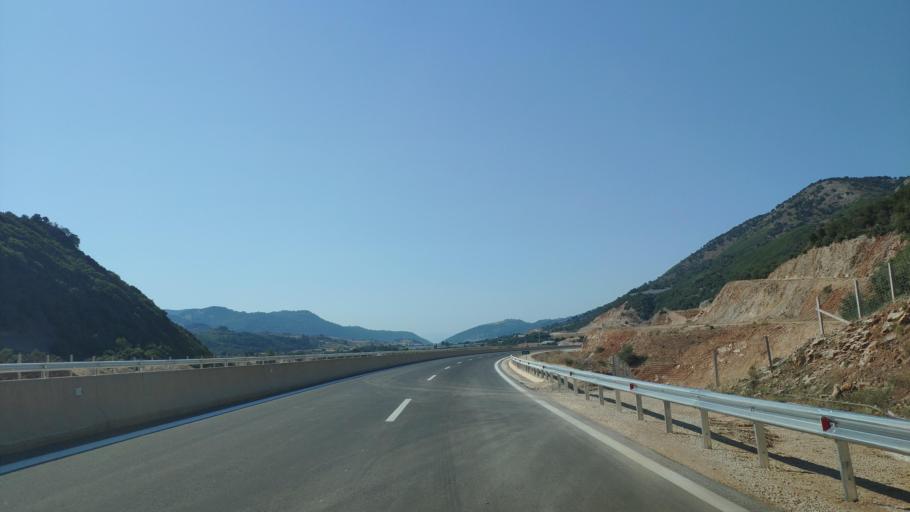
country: GR
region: West Greece
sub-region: Nomos Aitolias kai Akarnanias
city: Katouna
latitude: 38.7827
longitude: 21.1443
